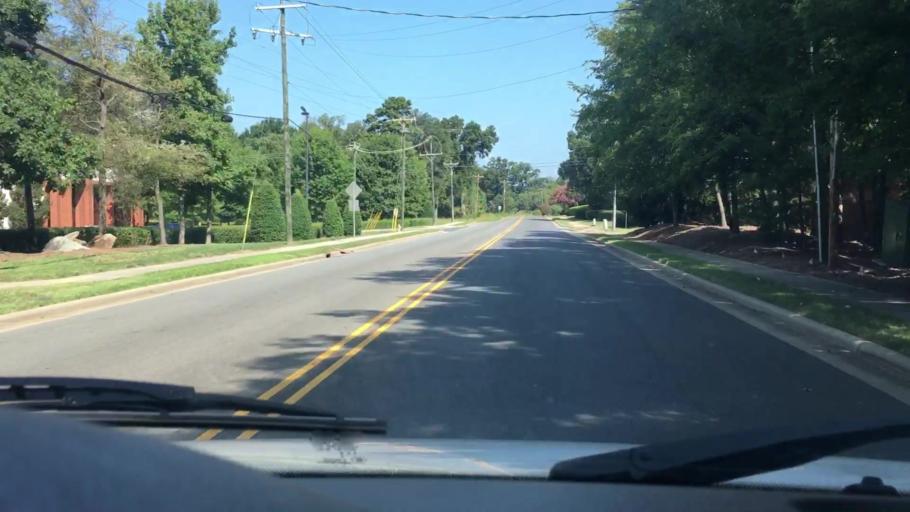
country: US
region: North Carolina
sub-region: Mecklenburg County
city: Charlotte
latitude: 35.3140
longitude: -80.8509
